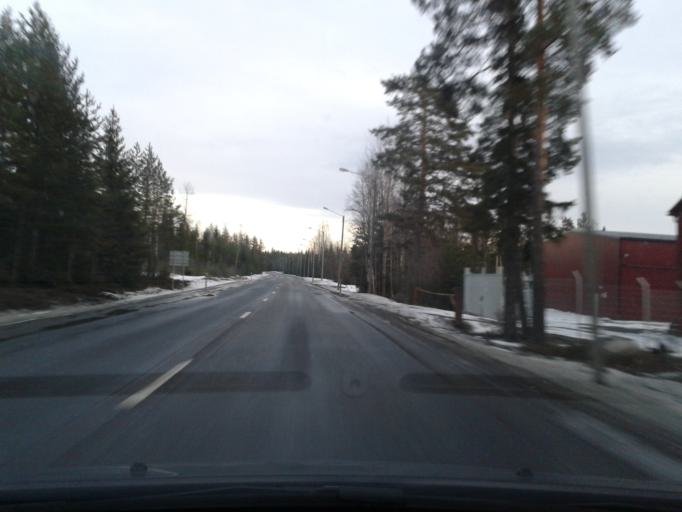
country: SE
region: Vaesternorrland
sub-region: Solleftea Kommun
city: Solleftea
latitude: 63.1520
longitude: 17.3339
